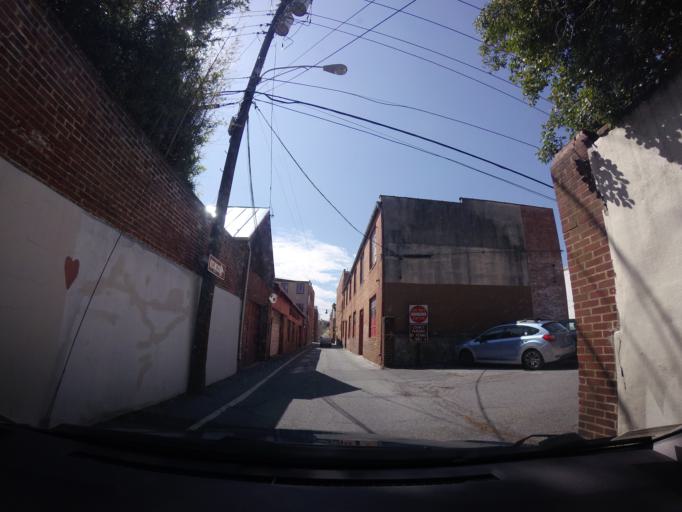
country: US
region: Maryland
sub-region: Frederick County
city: Frederick
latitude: 39.4147
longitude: -77.4090
